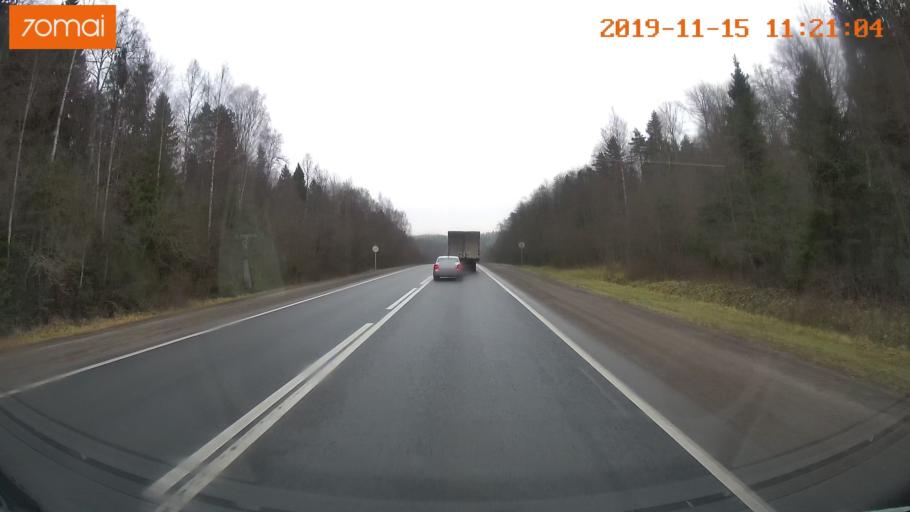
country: RU
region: Vologda
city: Molochnoye
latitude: 59.1433
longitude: 39.3286
